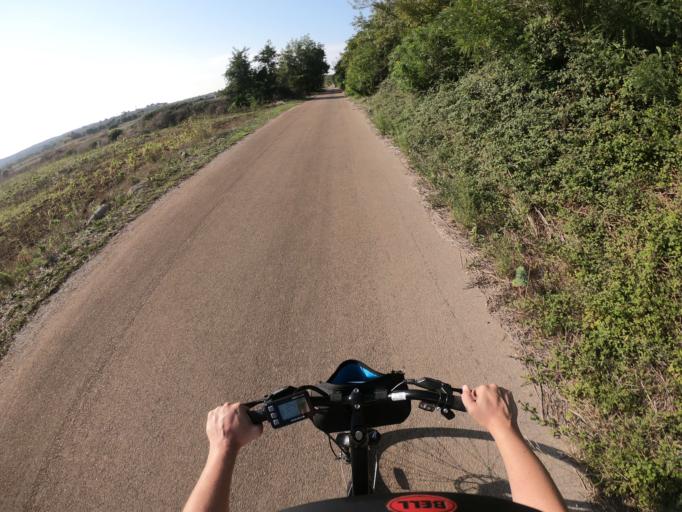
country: IT
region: Apulia
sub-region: Provincia di Lecce
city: Leuca
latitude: 39.8117
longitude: 18.3648
